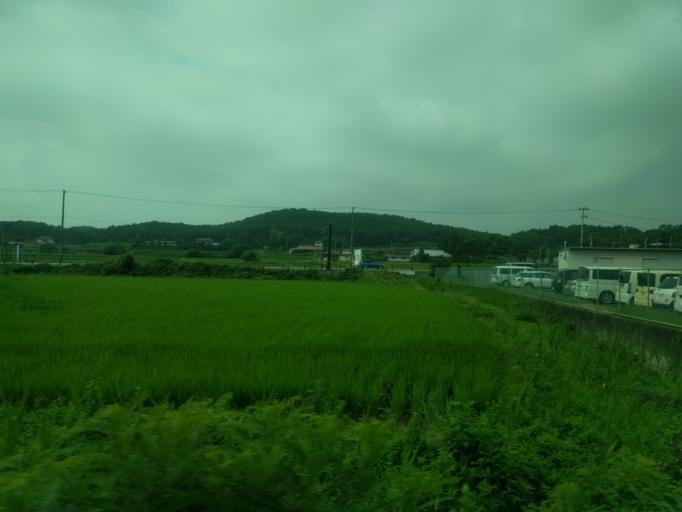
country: JP
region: Fukushima
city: Motomiya
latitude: 37.4743
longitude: 140.3035
